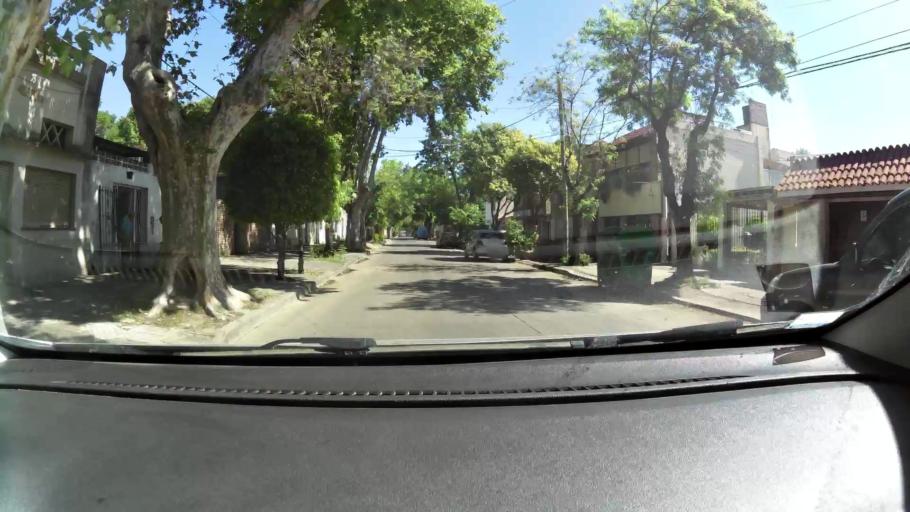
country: AR
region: Santa Fe
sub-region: Departamento de Rosario
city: Rosario
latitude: -32.9467
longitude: -60.6839
